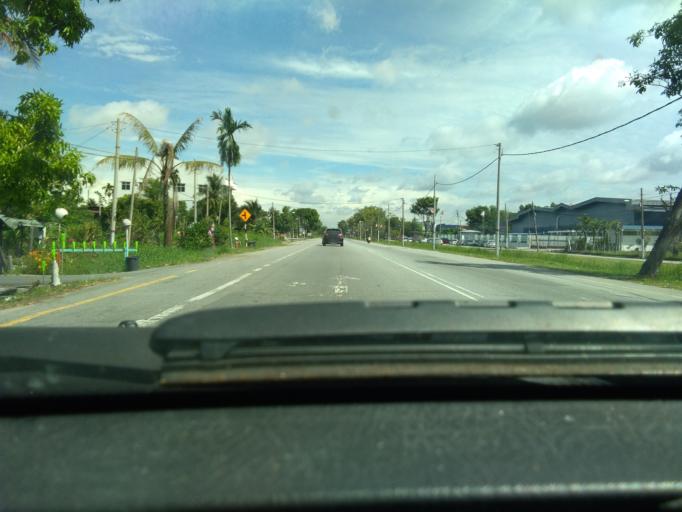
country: MY
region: Perak
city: Parit Buntar
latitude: 5.1029
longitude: 100.4865
